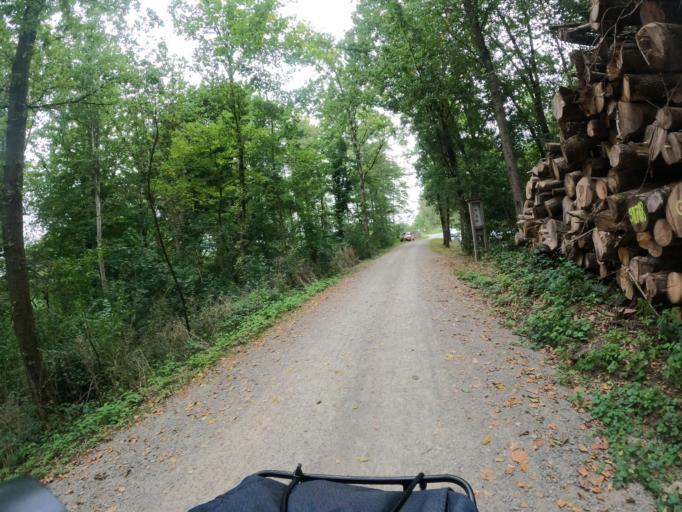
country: CH
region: Zurich
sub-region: Bezirk Affoltern
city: Ottenbach
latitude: 47.2786
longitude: 8.3932
